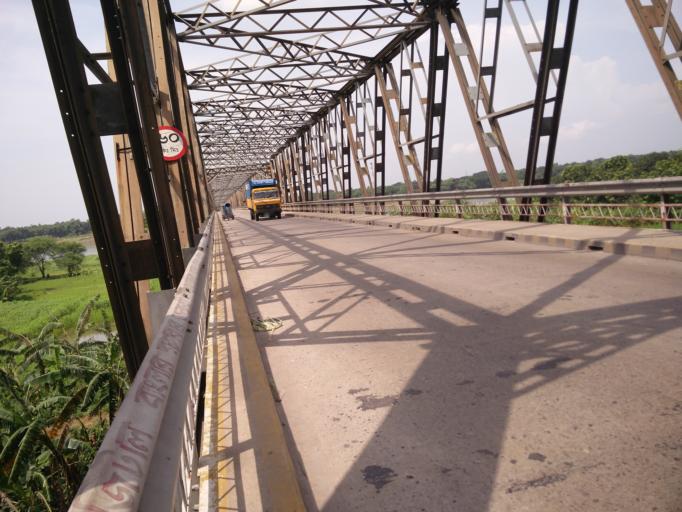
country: BD
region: Khulna
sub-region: Magura
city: Magura
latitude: 23.5442
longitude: 89.5180
